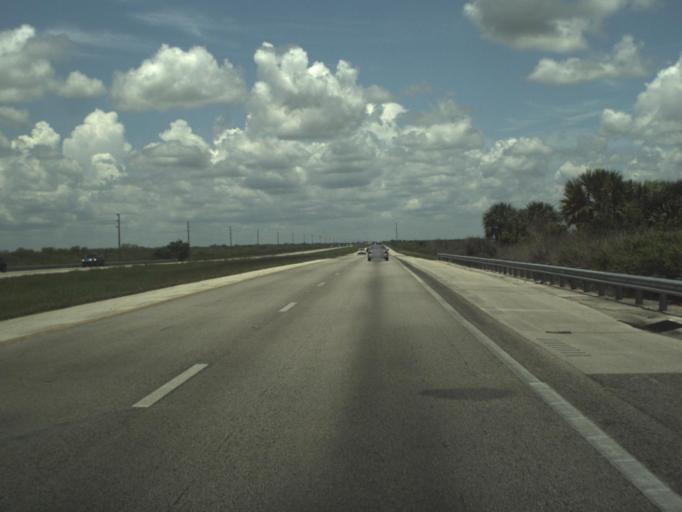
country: US
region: Florida
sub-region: Broward County
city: Weston
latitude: 26.1515
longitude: -80.7313
